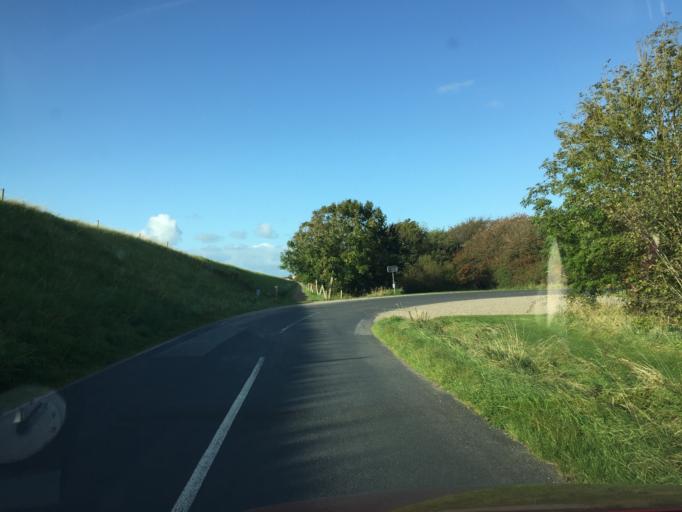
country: DE
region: Schleswig-Holstein
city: Klanxbull
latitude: 54.9584
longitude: 8.6835
